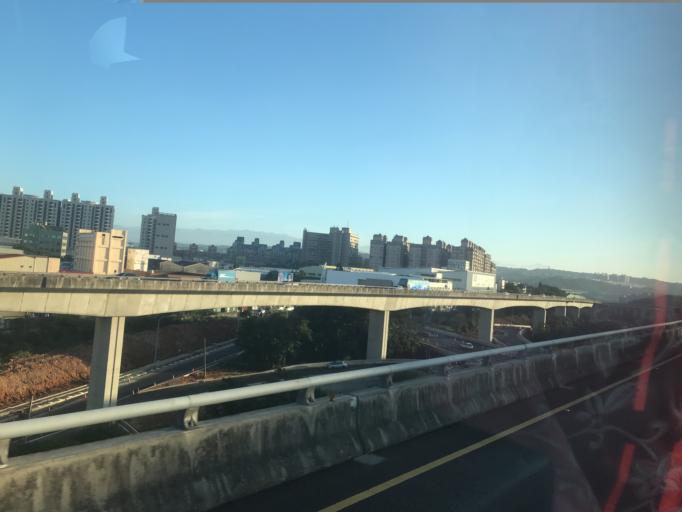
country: TW
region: Taiwan
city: Daxi
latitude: 24.9260
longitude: 121.1716
